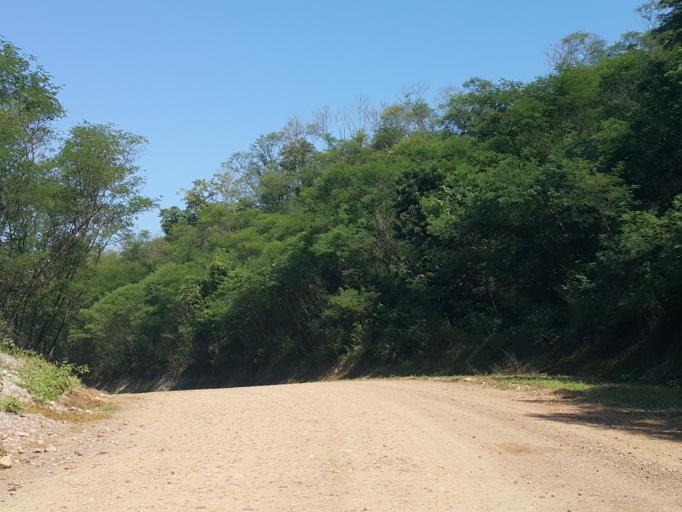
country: TH
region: Lampang
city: Mae Mo
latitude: 18.3273
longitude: 99.7398
